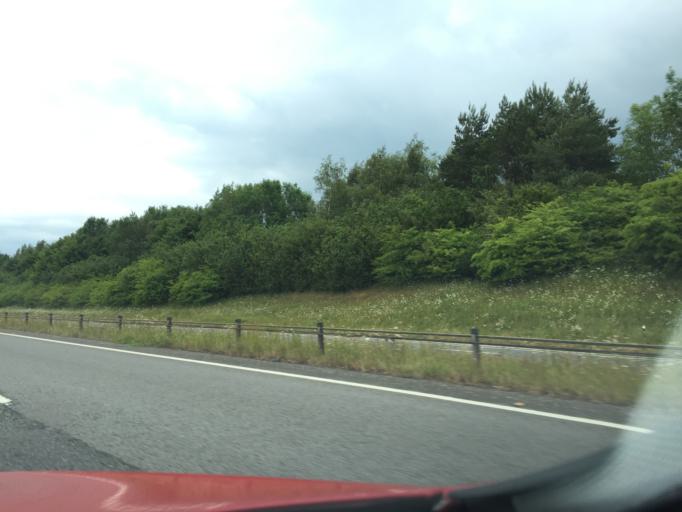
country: GB
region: England
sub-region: Gloucestershire
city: Coates
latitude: 51.7866
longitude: -2.0414
